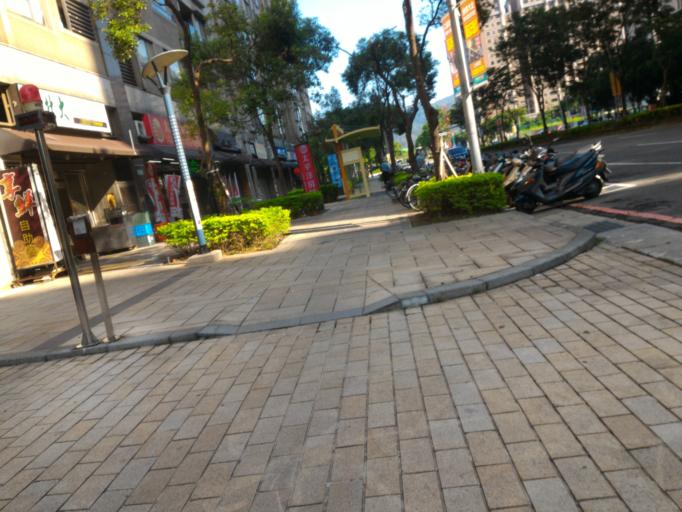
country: TW
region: Taiwan
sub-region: Taoyuan
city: Taoyuan
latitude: 24.9461
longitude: 121.3776
